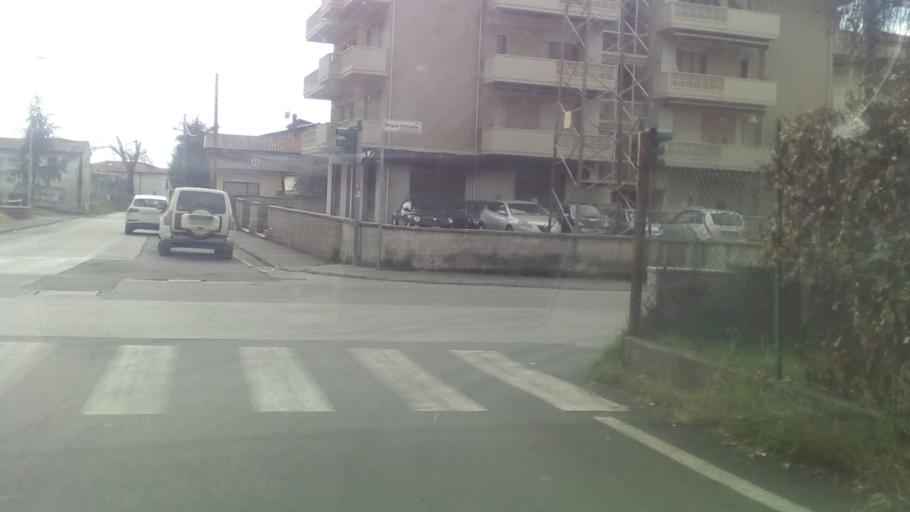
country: IT
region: Tuscany
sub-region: Provincia di Massa-Carrara
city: Carrara
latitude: 44.0584
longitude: 10.0714
